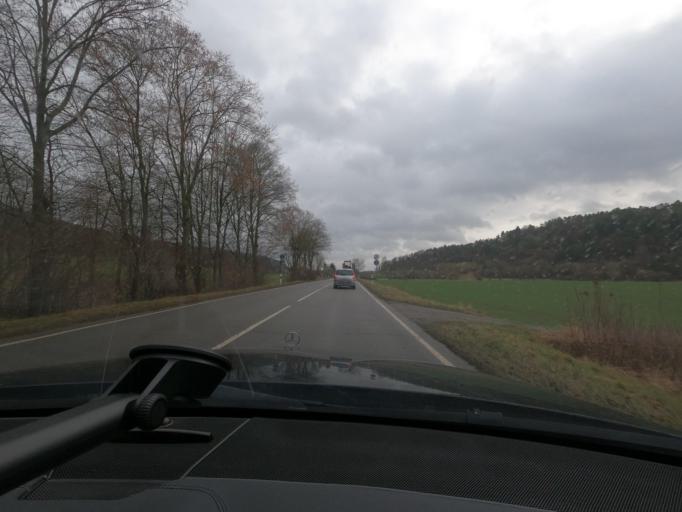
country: DE
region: Hesse
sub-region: Regierungsbezirk Kassel
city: Volkmarsen
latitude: 51.4040
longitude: 9.1380
